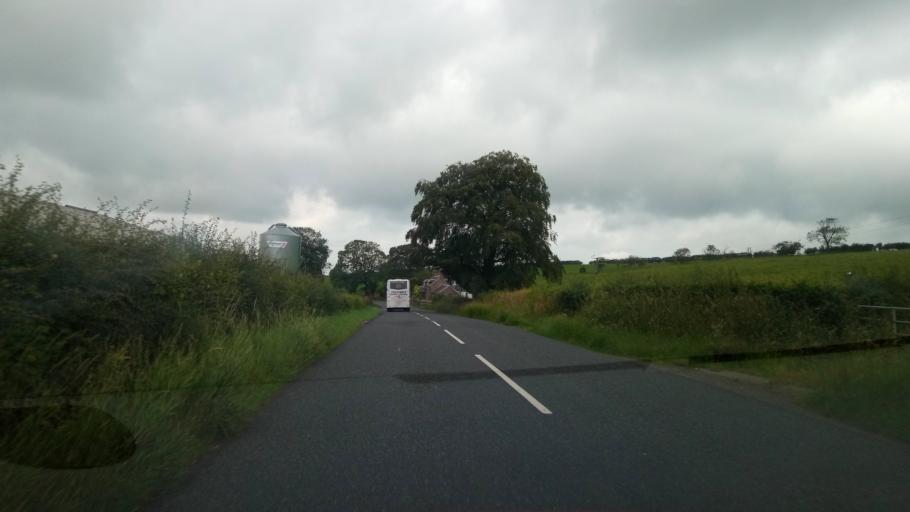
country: GB
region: Scotland
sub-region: Dumfries and Galloway
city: Langholm
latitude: 55.0955
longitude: -2.8982
